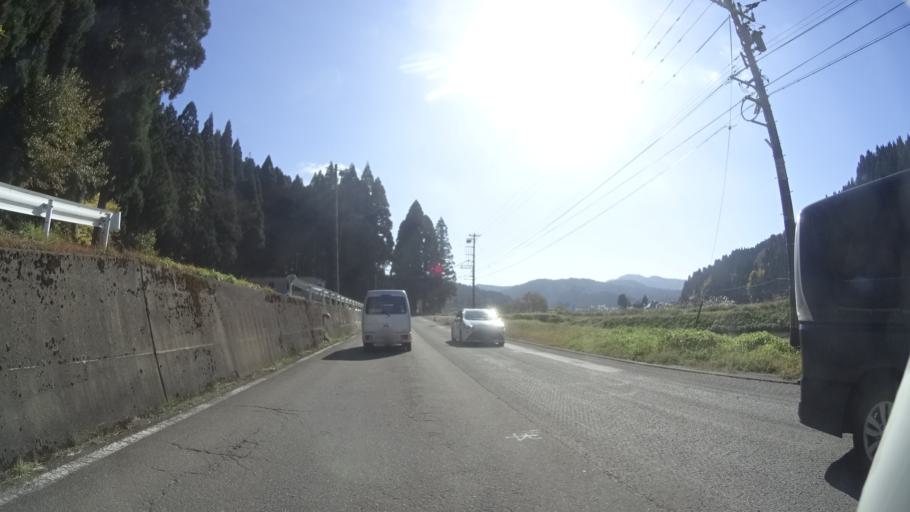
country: JP
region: Fukui
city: Ono
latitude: 35.9123
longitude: 136.3549
